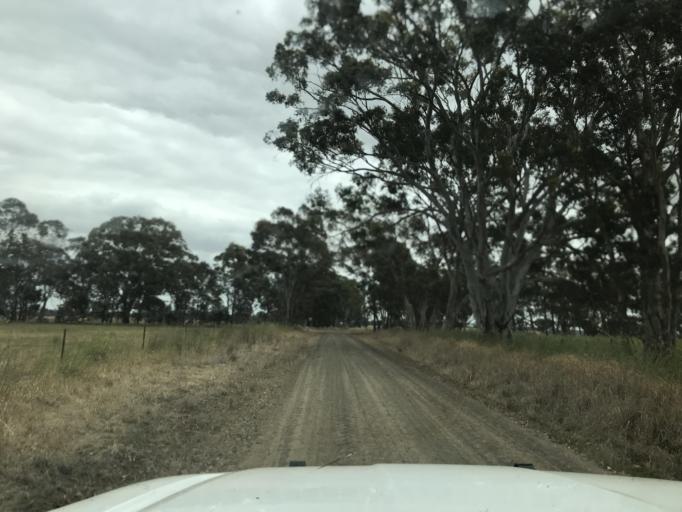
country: AU
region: South Australia
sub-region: Naracoorte and Lucindale
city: Naracoorte
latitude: -36.9471
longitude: 141.3095
